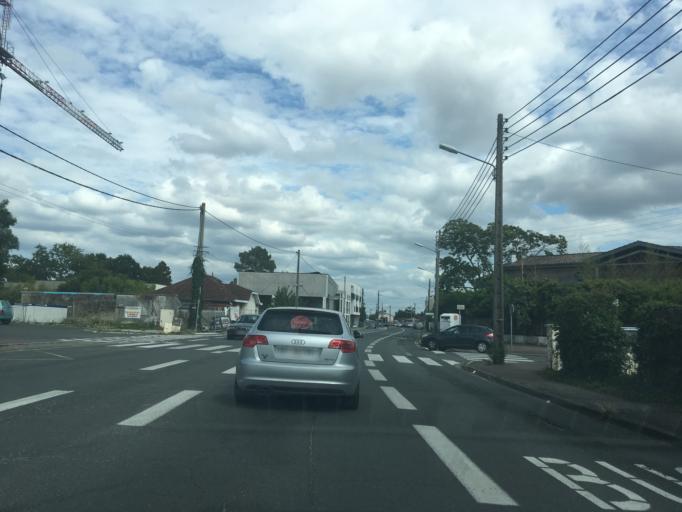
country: FR
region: Aquitaine
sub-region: Departement de la Gironde
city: Eysines
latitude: 44.8623
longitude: -0.6455
